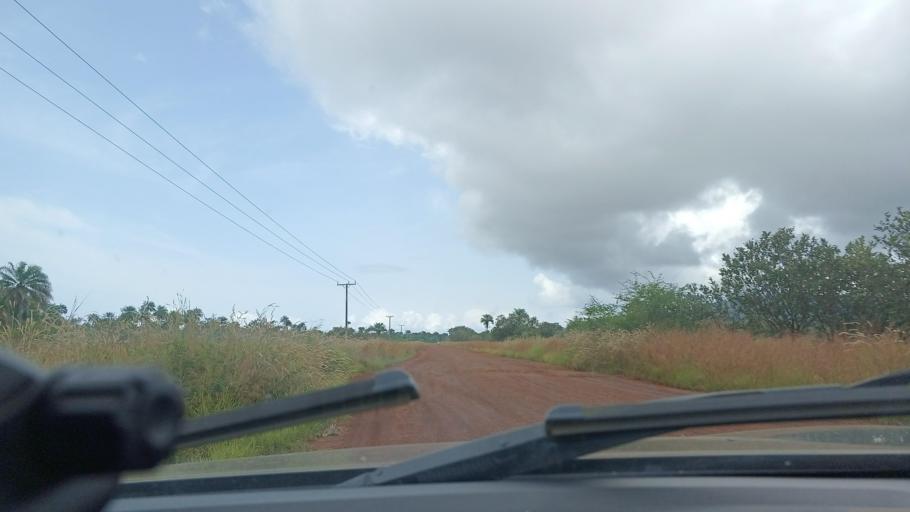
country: LR
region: Grand Cape Mount
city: Robertsport
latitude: 6.7033
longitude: -11.3138
